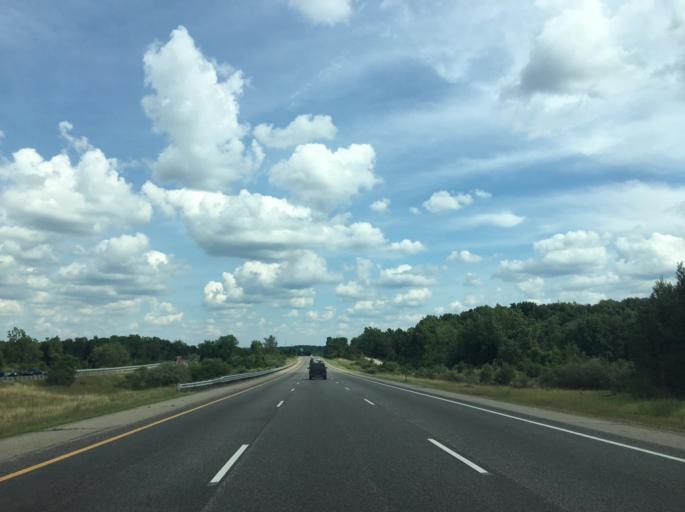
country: US
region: Michigan
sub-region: Genesee County
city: Grand Blanc
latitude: 42.8786
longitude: -83.6084
